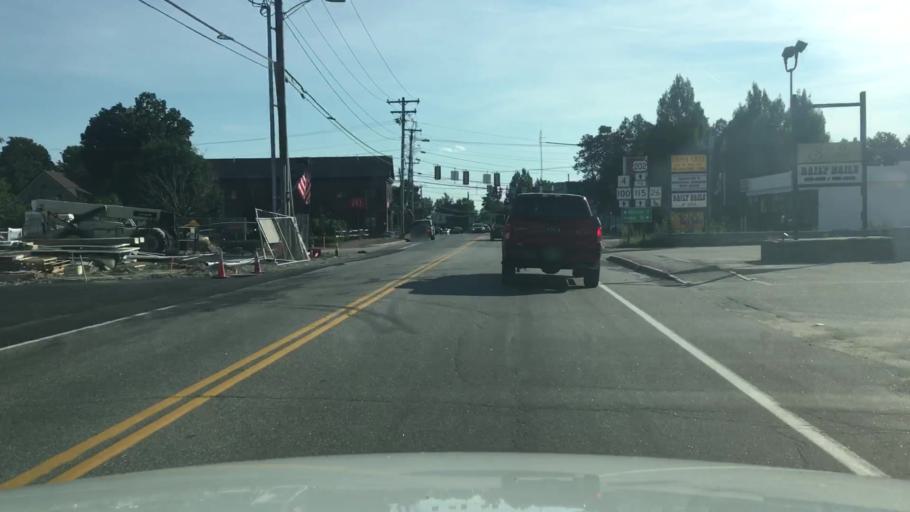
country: US
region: Maine
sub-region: Cumberland County
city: New Gloucester
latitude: 43.8867
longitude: -70.3296
